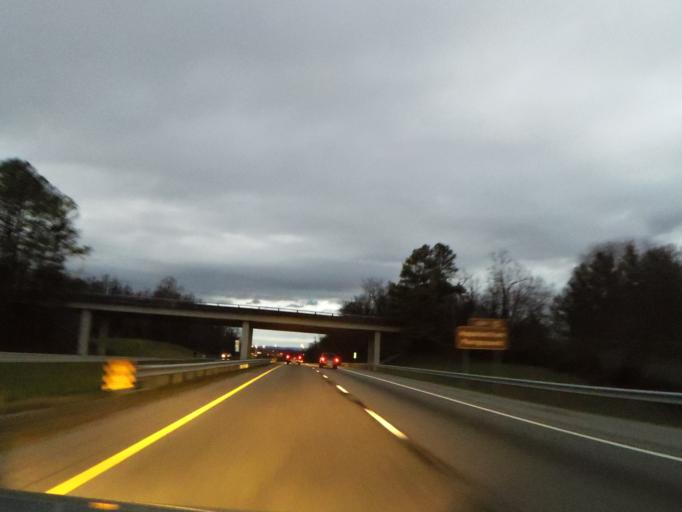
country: US
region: Tennessee
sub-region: Washington County
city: Gray
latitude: 36.3992
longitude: -82.4630
